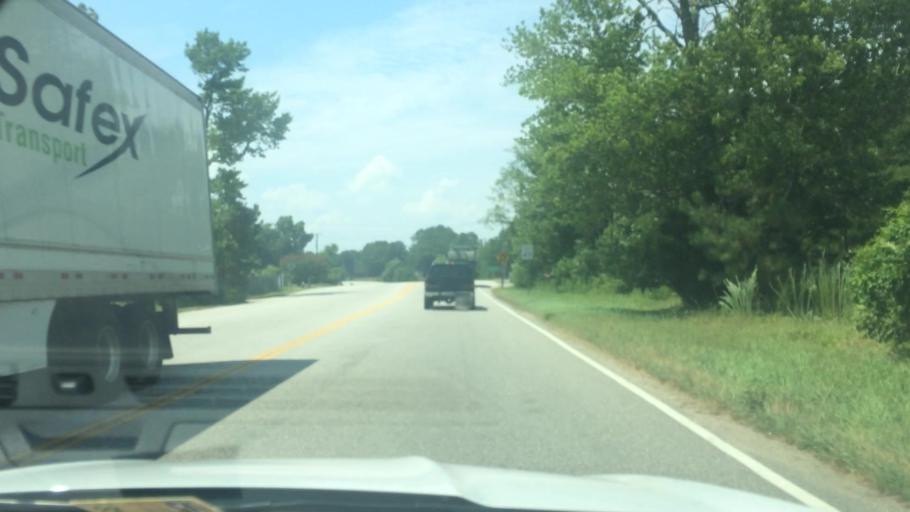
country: US
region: Virginia
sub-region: City of Williamsburg
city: Williamsburg
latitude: 37.2342
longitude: -76.6294
